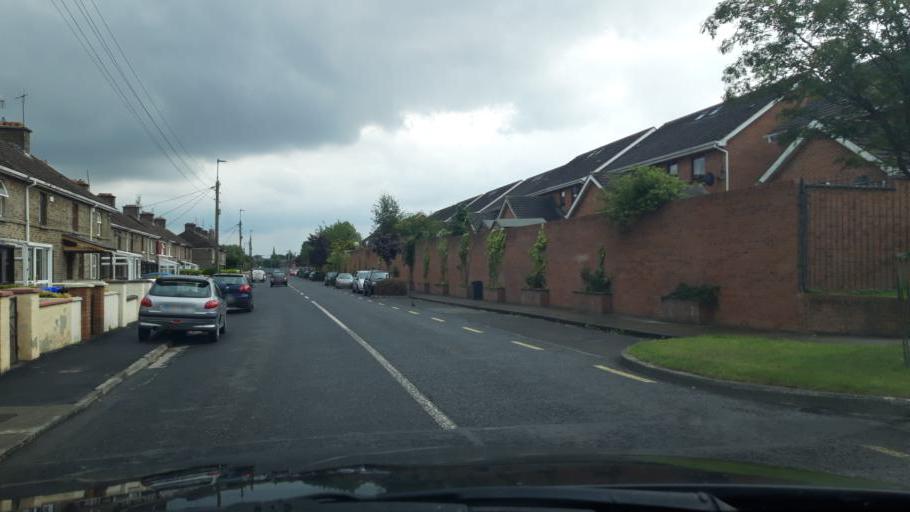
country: IE
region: Leinster
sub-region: Kildare
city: Athy
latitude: 52.9990
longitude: -6.9878
